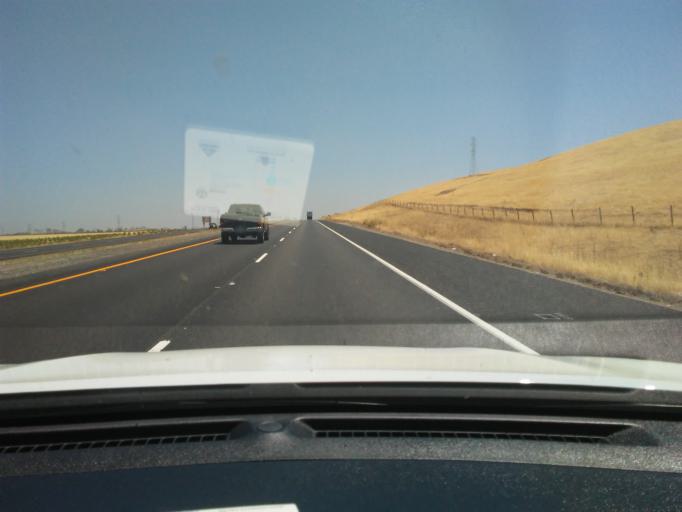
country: US
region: California
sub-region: San Joaquin County
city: Tracy
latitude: 37.6274
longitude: -121.3836
